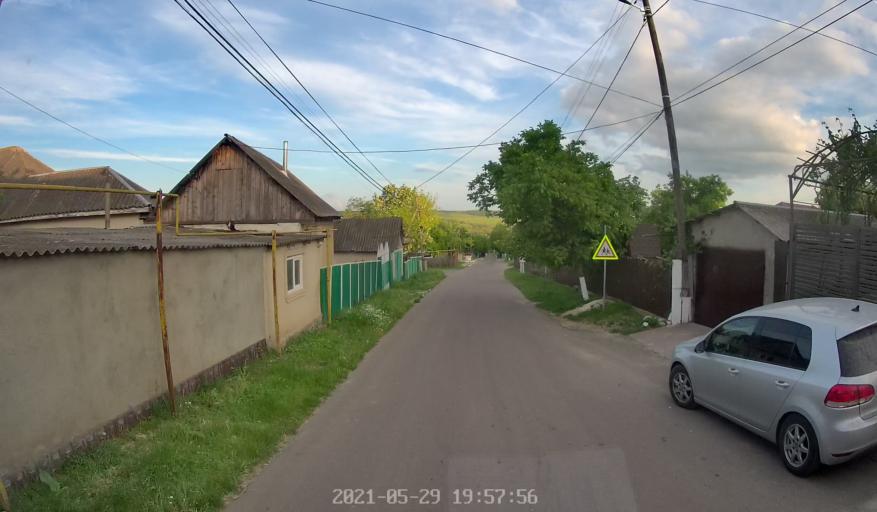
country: MD
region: Chisinau
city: Singera
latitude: 46.8317
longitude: 28.9724
